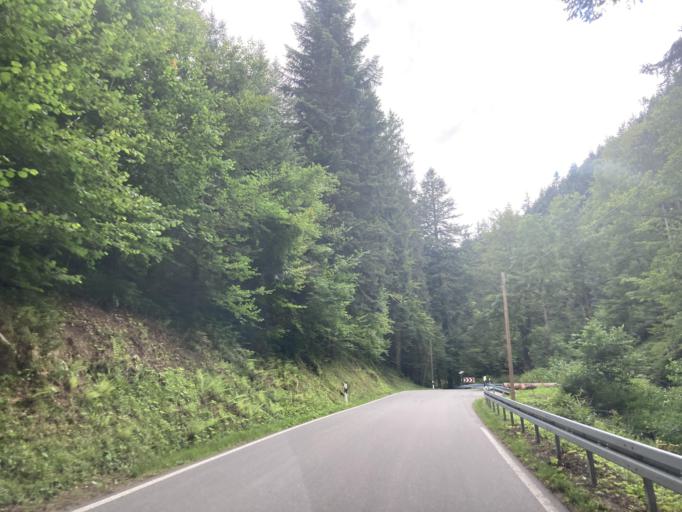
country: DE
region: Baden-Wuerttemberg
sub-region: Freiburg Region
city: Schonach im Schwarzwald
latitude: 48.1779
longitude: 8.1599
